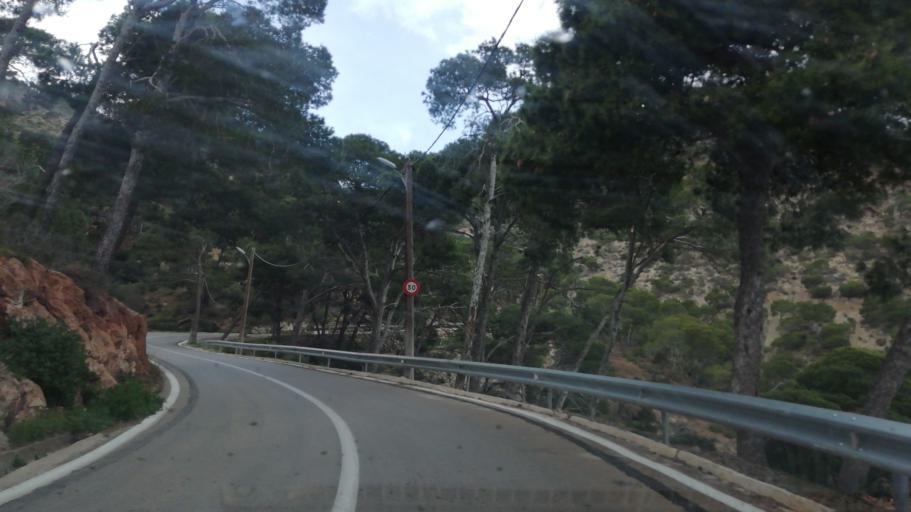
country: DZ
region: Oran
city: Oran
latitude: 35.7050
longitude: -0.6631
